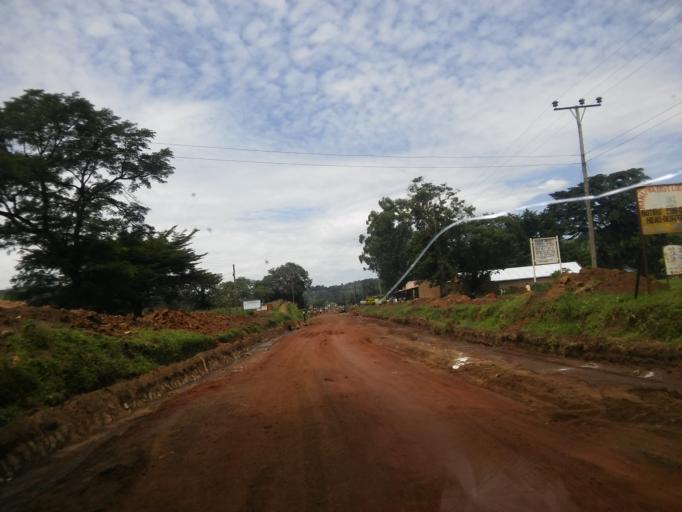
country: UG
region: Eastern Region
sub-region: Tororo District
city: Tororo
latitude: 0.8256
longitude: 34.2911
